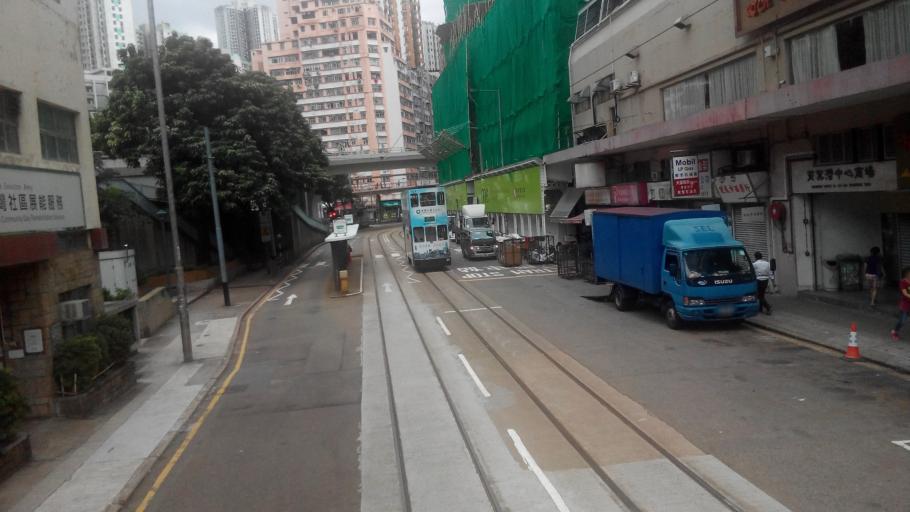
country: HK
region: Wanchai
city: Wan Chai
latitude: 22.2767
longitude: 114.2295
